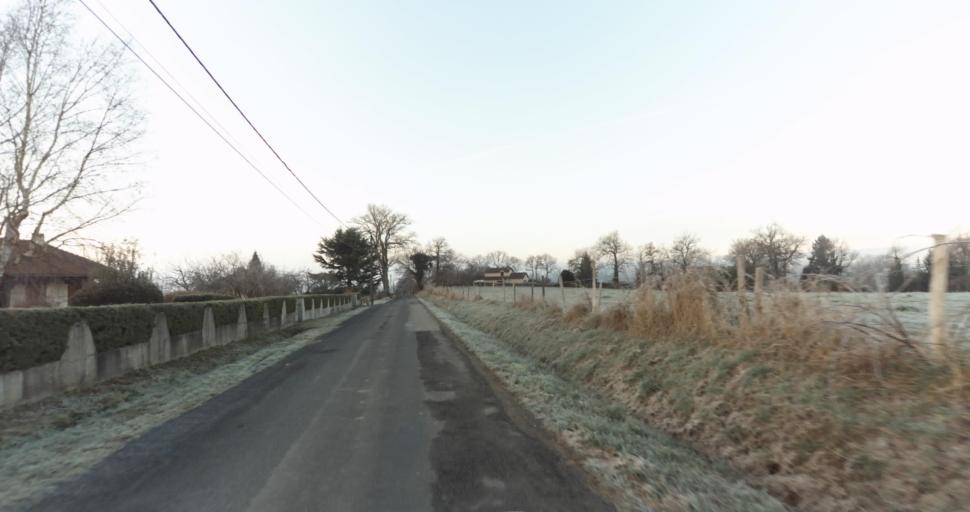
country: FR
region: Limousin
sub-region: Departement de la Haute-Vienne
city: Aixe-sur-Vienne
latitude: 45.8056
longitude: 1.1286
